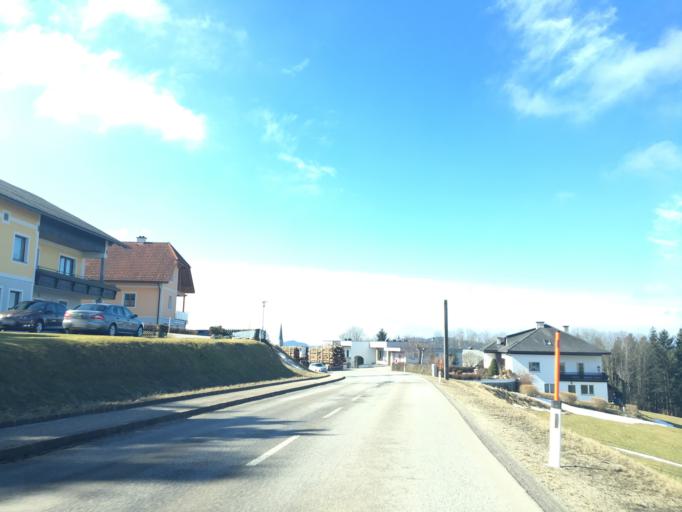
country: AT
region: Upper Austria
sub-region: Politischer Bezirk Perg
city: Sankt Georgen am Walde
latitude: 48.3625
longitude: 14.9038
